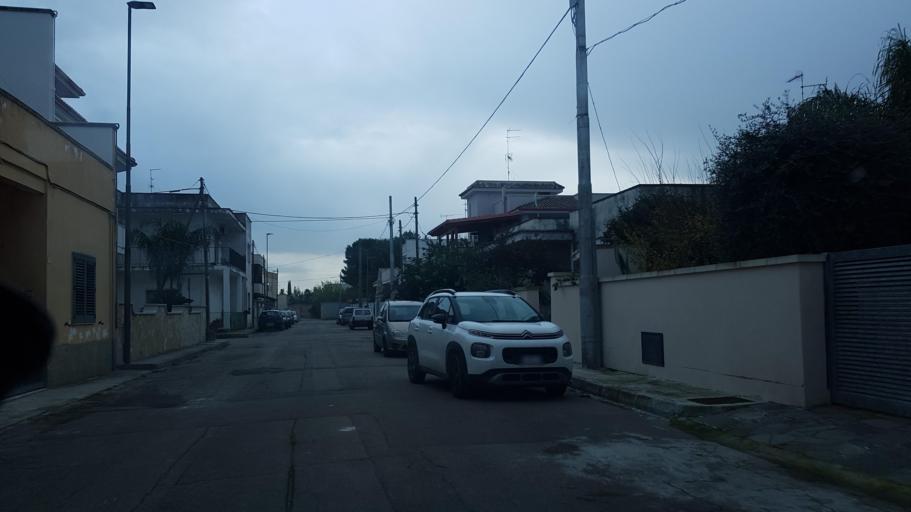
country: IT
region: Apulia
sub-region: Provincia di Lecce
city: Merine
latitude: 40.3299
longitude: 18.2222
